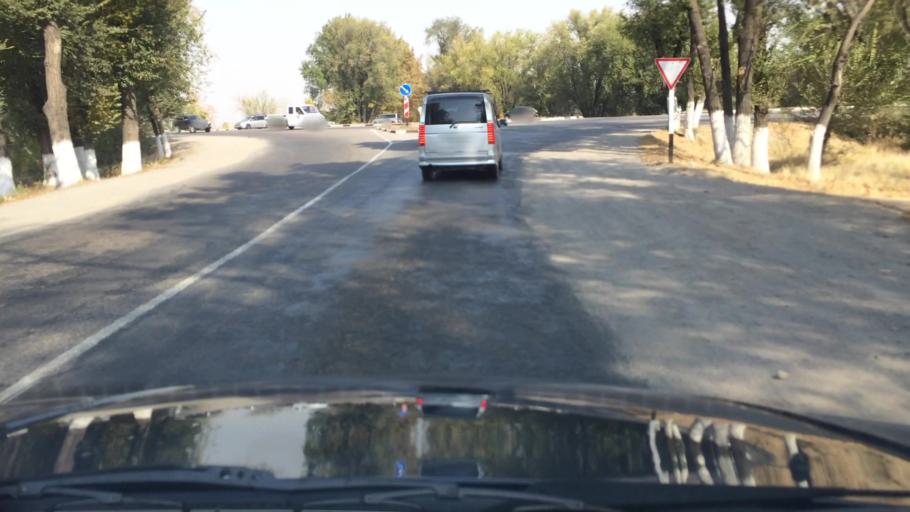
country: KG
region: Chuy
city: Lebedinovka
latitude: 42.9297
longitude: 74.6912
